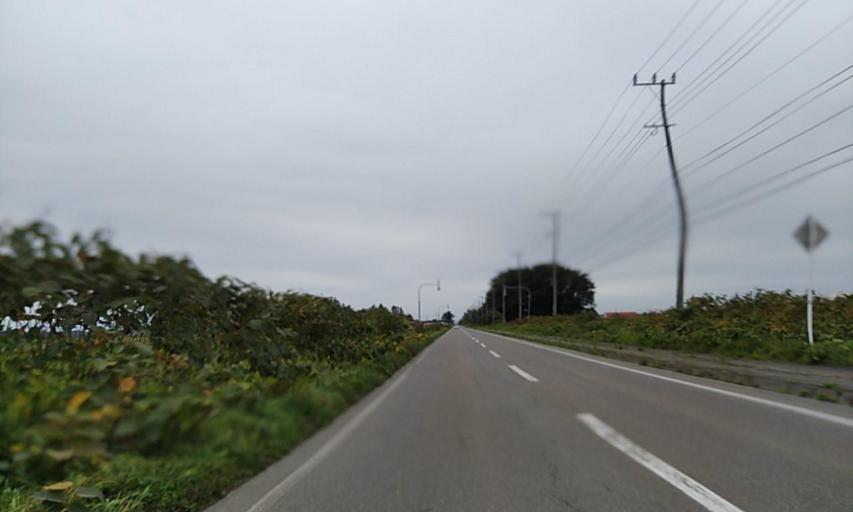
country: JP
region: Hokkaido
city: Obihiro
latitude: 42.6677
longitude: 143.1120
